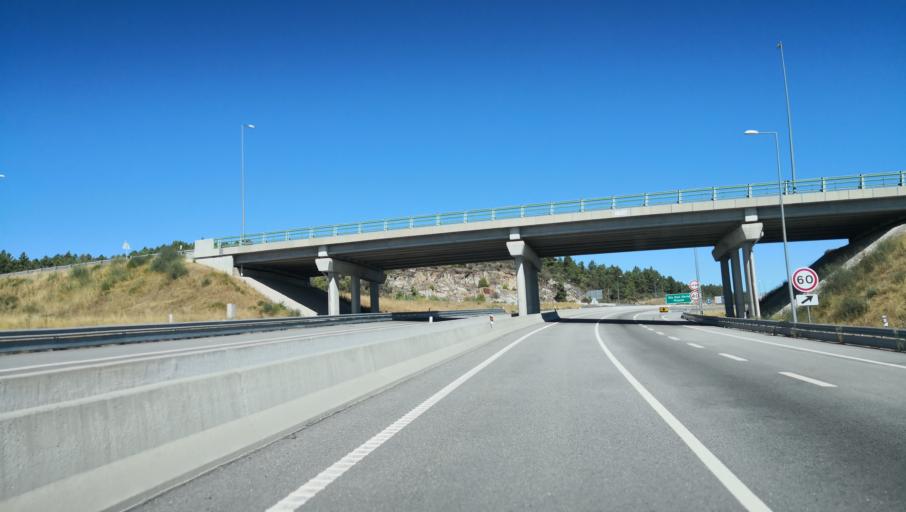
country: PT
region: Vila Real
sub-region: Vila Real
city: Vila Real
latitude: 41.3172
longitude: -7.6611
